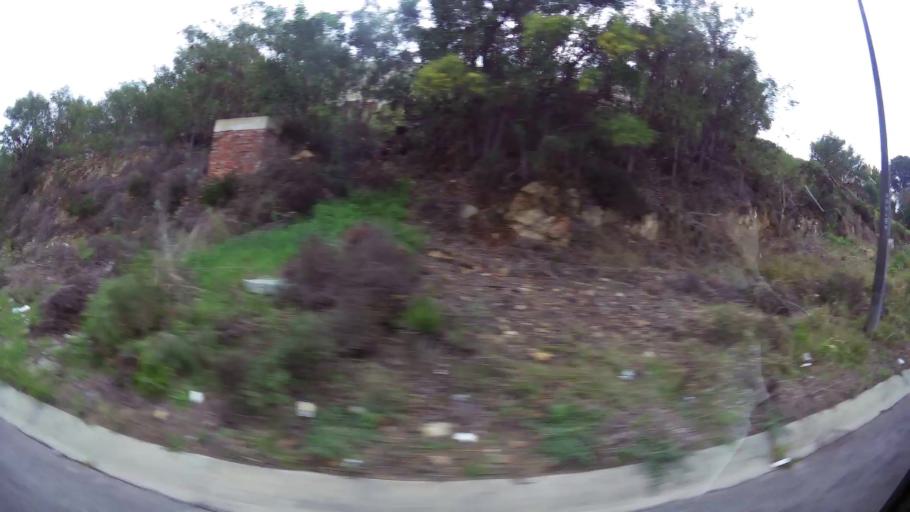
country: ZA
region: Eastern Cape
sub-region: Nelson Mandela Bay Metropolitan Municipality
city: Port Elizabeth
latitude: -33.9351
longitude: 25.5203
